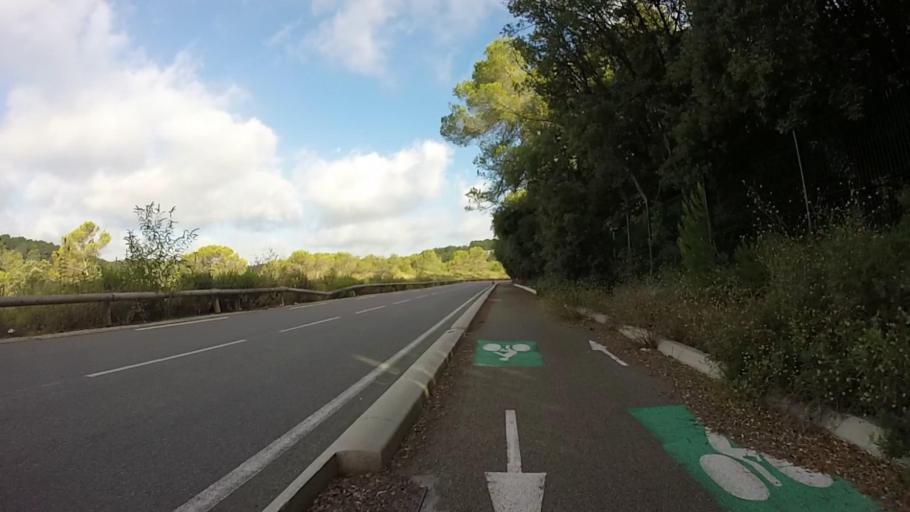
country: FR
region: Provence-Alpes-Cote d'Azur
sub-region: Departement des Alpes-Maritimes
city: Biot
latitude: 43.6122
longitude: 7.0754
